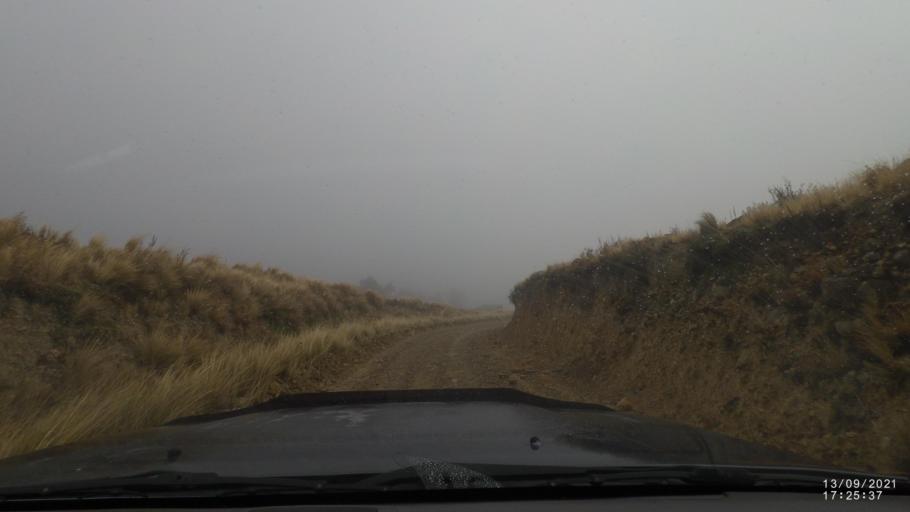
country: BO
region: Cochabamba
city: Colomi
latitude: -17.3593
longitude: -65.7814
